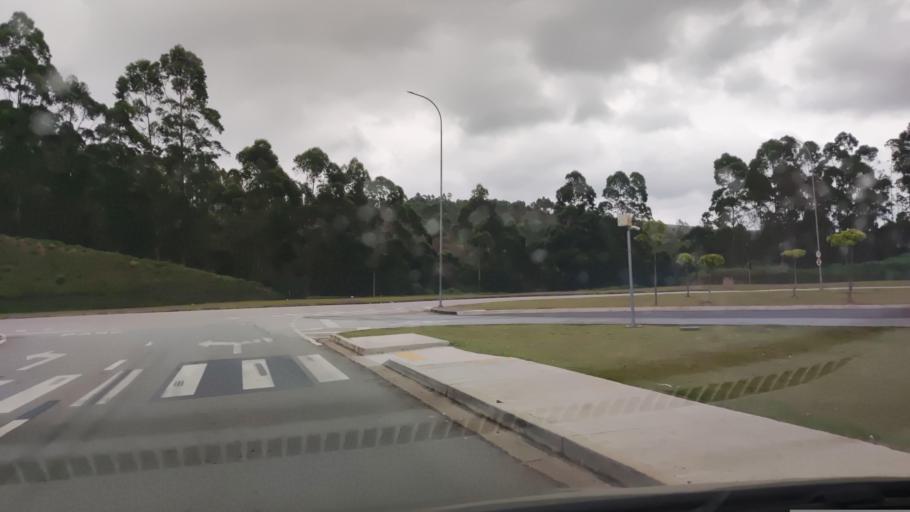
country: BR
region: Sao Paulo
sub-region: Cajamar
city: Cajamar
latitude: -23.3292
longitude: -46.8520
